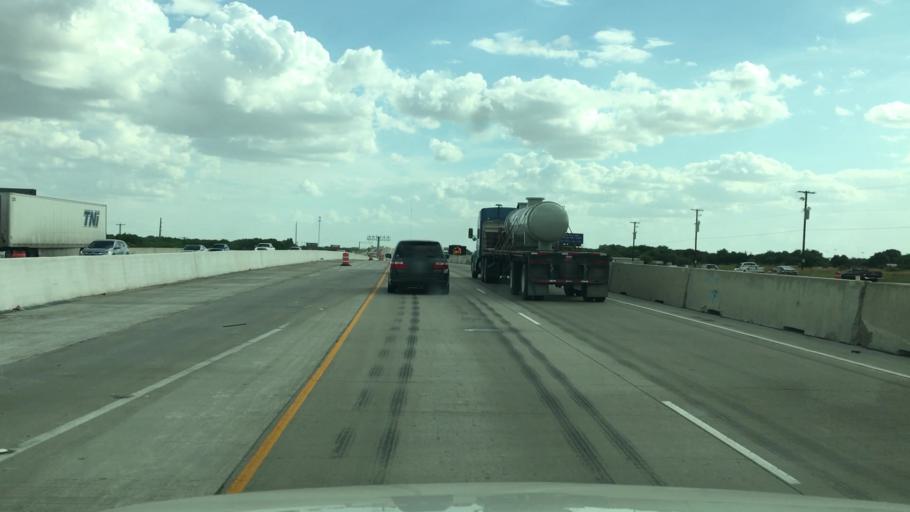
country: US
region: Texas
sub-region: McLennan County
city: Bruceville-Eddy
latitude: 31.3165
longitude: -97.2393
